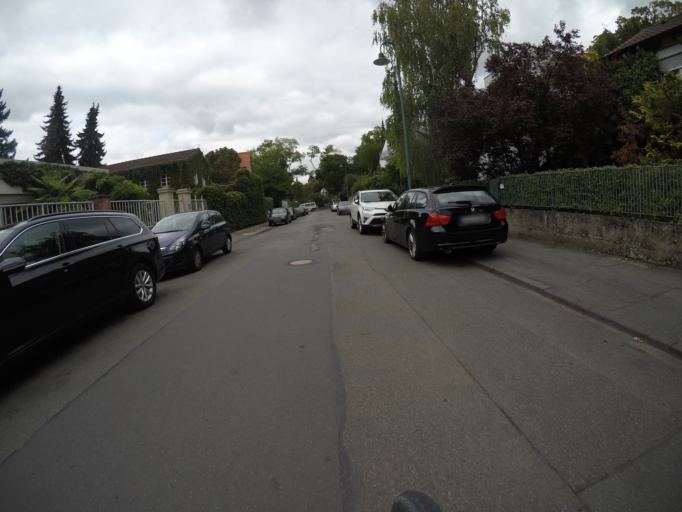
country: DE
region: Hesse
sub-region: Regierungsbezirk Darmstadt
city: Darmstadt
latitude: 49.8640
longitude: 8.6504
